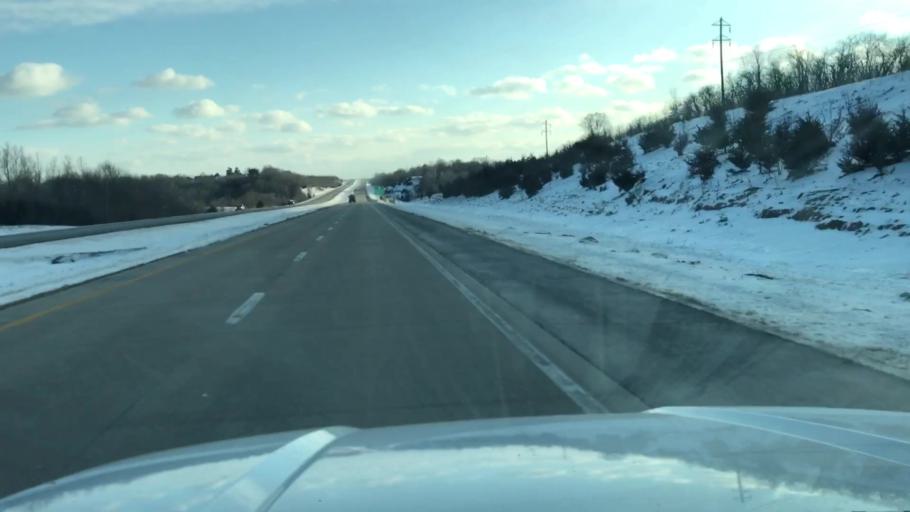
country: US
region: Missouri
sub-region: Andrew County
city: Savannah
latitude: 39.9439
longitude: -94.8603
